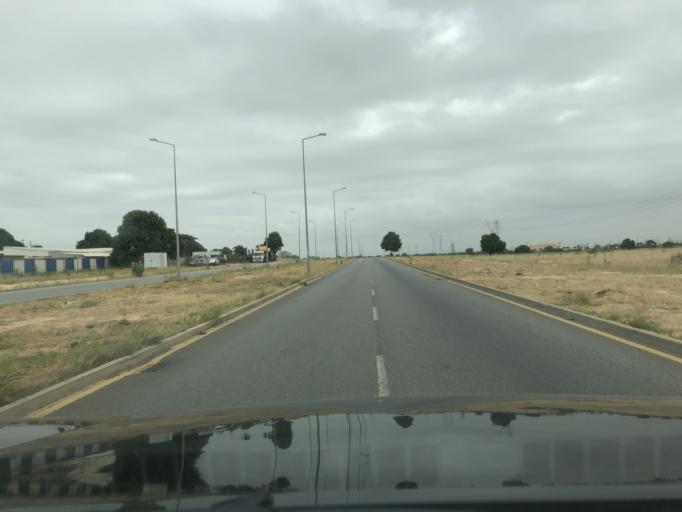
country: AO
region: Luanda
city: Luanda
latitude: -8.9757
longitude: 13.2826
